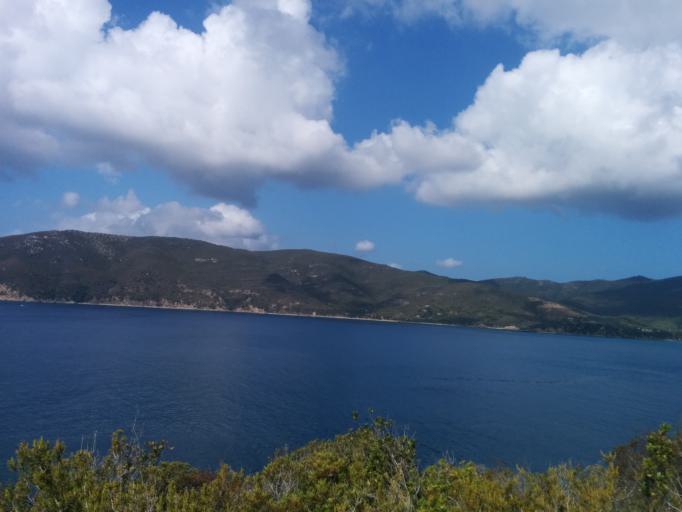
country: IT
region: Tuscany
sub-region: Provincia di Livorno
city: Capoliveri
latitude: 42.7459
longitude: 10.3151
